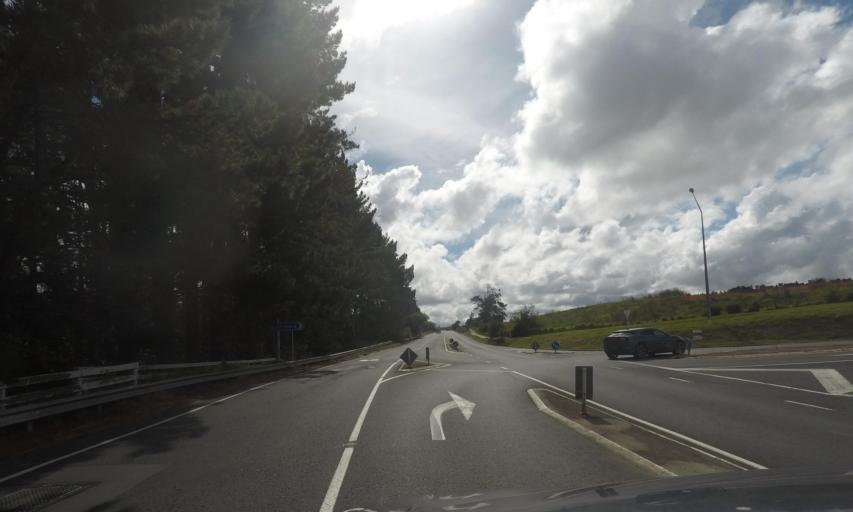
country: NZ
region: Auckland
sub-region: Auckland
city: Rosebank
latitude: -36.7991
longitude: 174.6338
